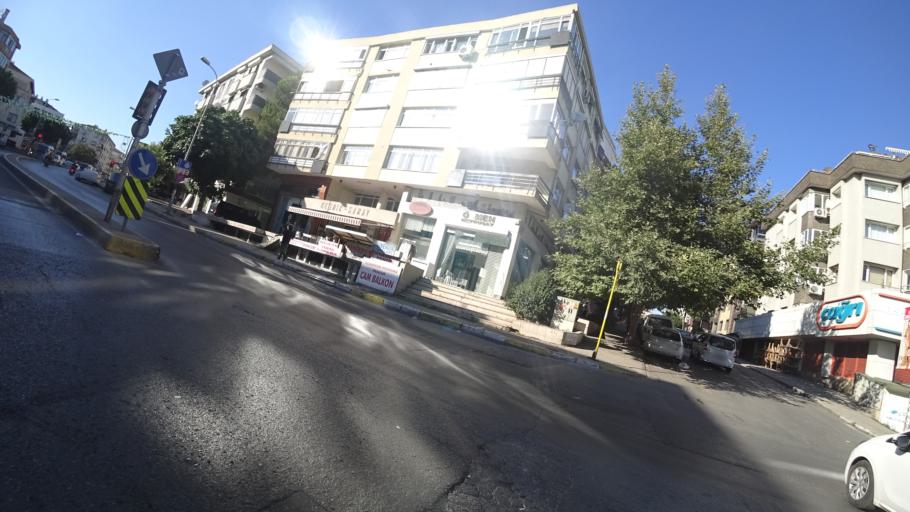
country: TR
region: Istanbul
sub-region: Atasehir
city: Atasehir
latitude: 40.9472
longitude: 29.1075
